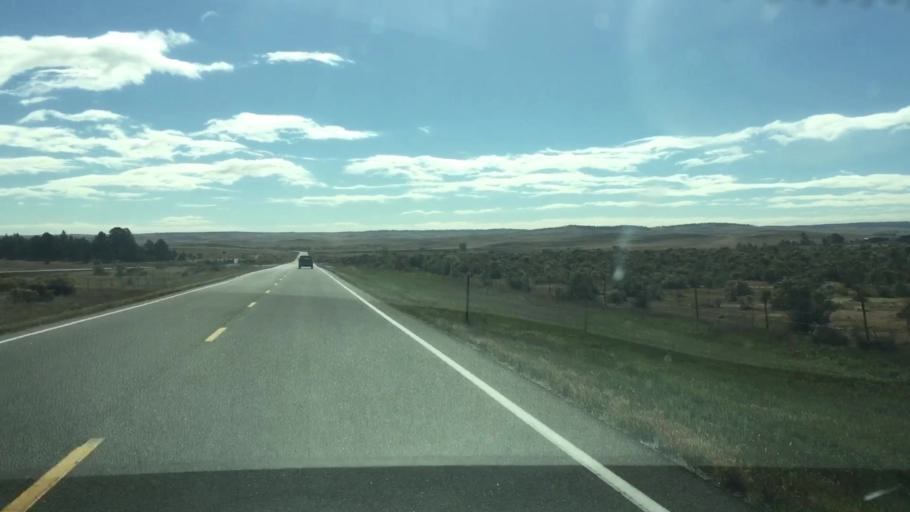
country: US
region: Colorado
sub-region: Elbert County
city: Kiowa
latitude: 39.3050
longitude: -104.3498
